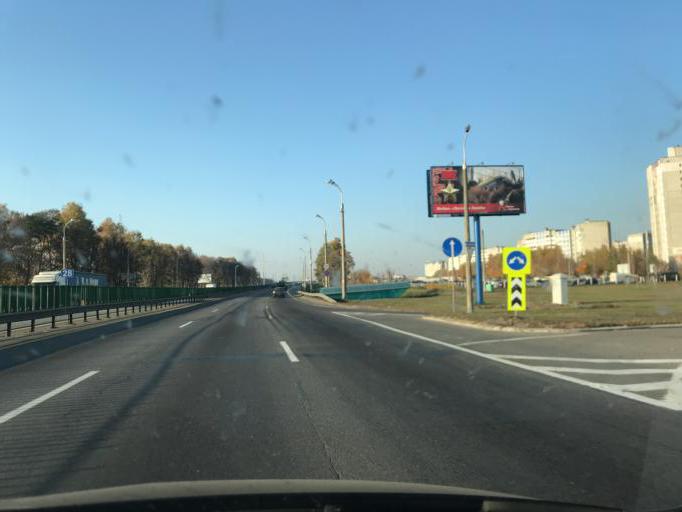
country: BY
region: Minsk
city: Malinovka
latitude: 53.8542
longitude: 27.4317
